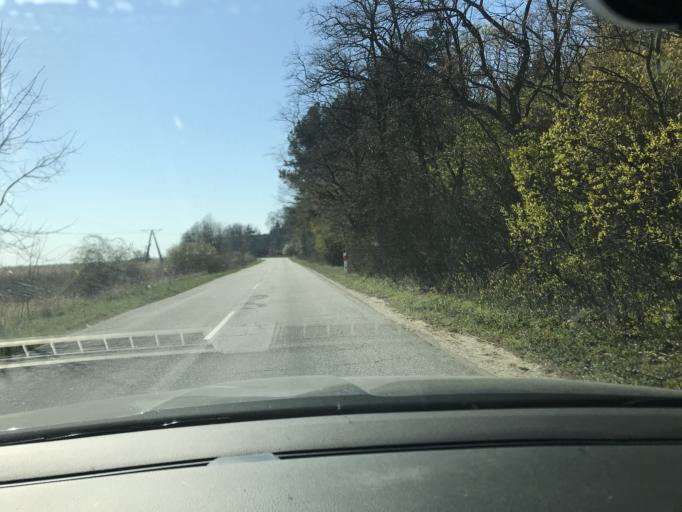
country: PL
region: Pomeranian Voivodeship
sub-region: Powiat nowodworski
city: Sztutowo
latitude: 54.3519
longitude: 19.2891
